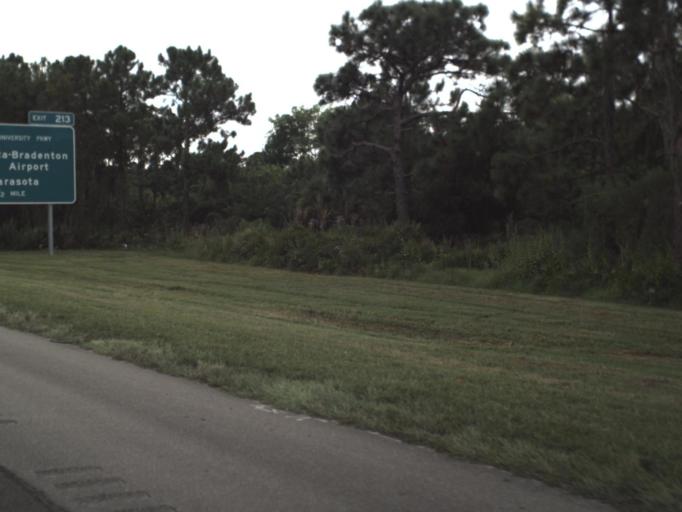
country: US
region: Florida
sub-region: Sarasota County
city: The Meadows
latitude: 27.4020
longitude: -82.4528
